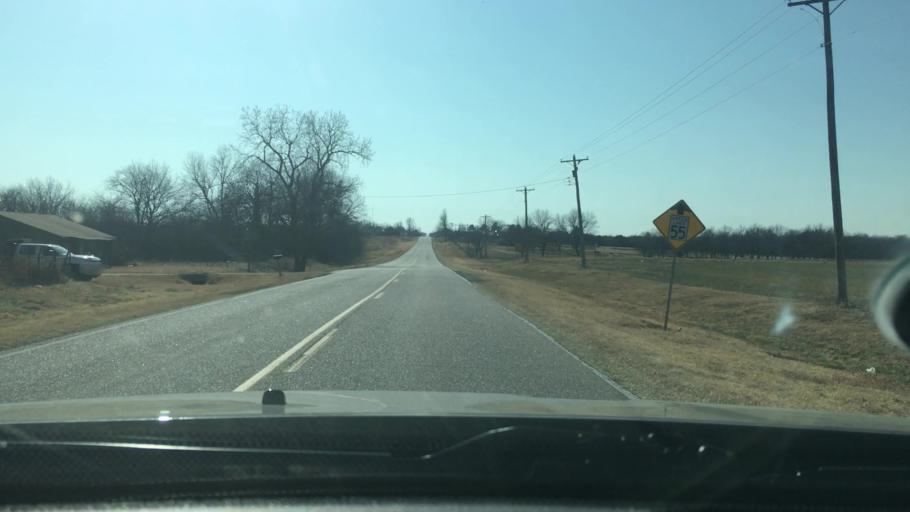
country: US
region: Oklahoma
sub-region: Garvin County
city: Stratford
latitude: 34.8087
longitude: -96.9677
